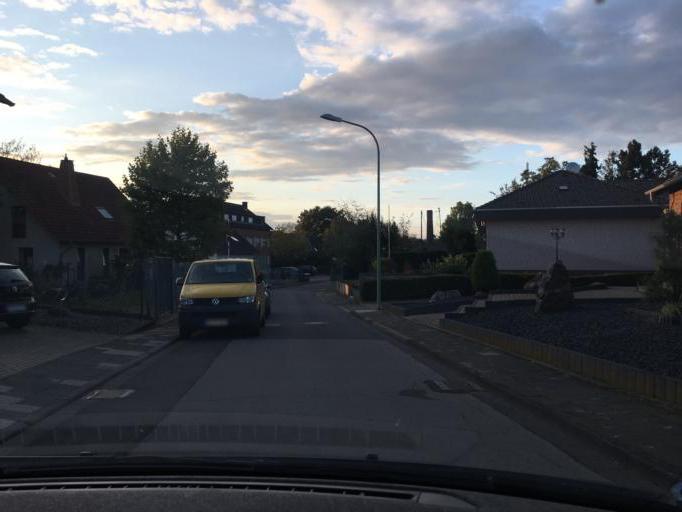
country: DE
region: North Rhine-Westphalia
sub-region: Regierungsbezirk Koln
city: Niederzier
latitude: 50.8684
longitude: 6.4710
